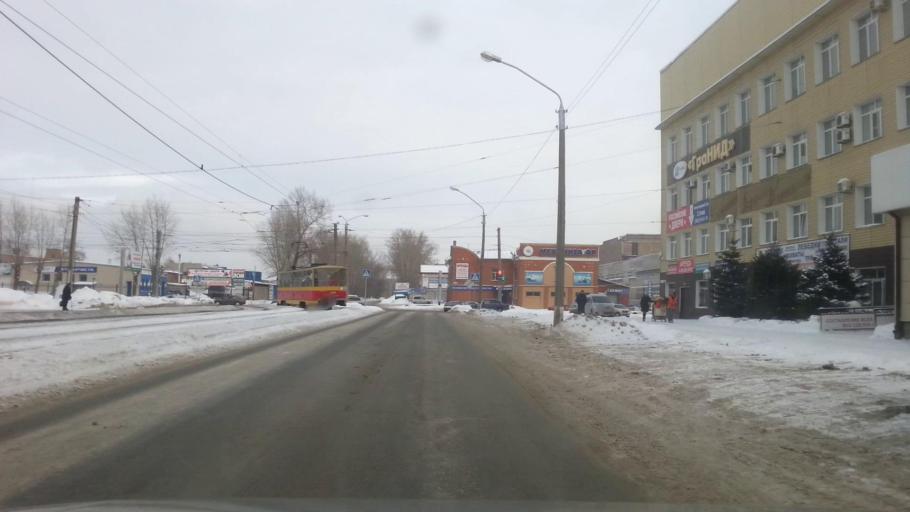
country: RU
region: Altai Krai
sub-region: Gorod Barnaulskiy
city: Barnaul
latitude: 53.3750
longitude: 83.7543
